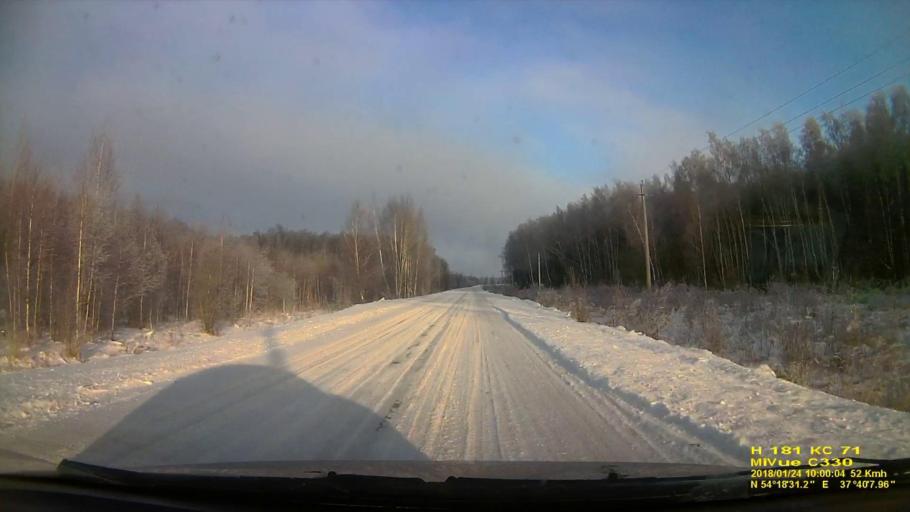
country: RU
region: Tula
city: Revyakino
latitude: 54.3087
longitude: 37.6689
